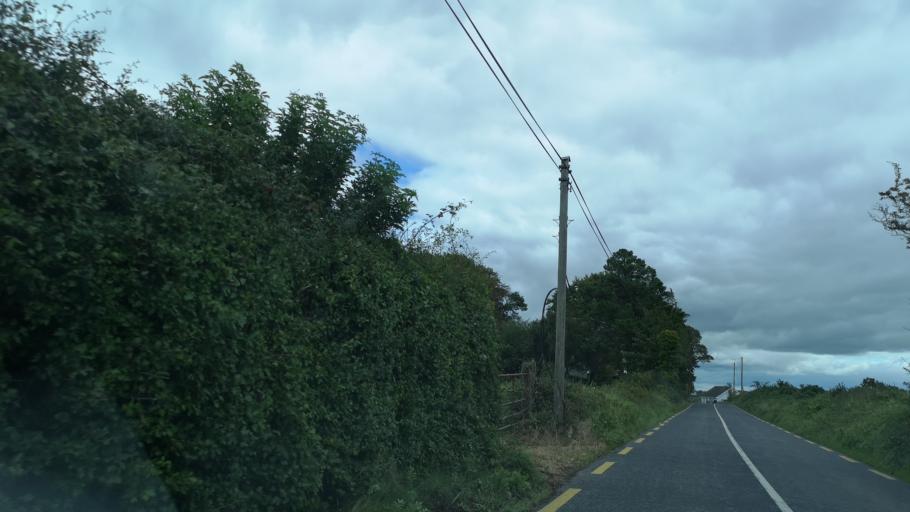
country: IE
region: Connaught
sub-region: County Galway
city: Ballinasloe
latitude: 53.2956
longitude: -8.1091
